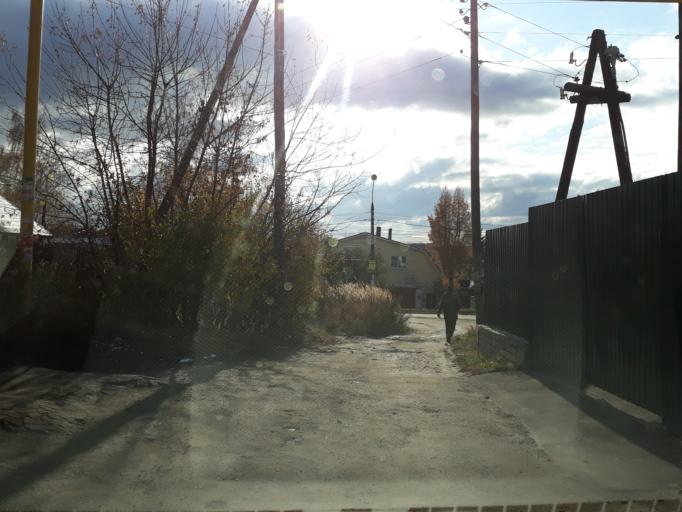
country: RU
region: Nizjnij Novgorod
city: Afonino
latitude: 56.2330
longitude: 44.0071
